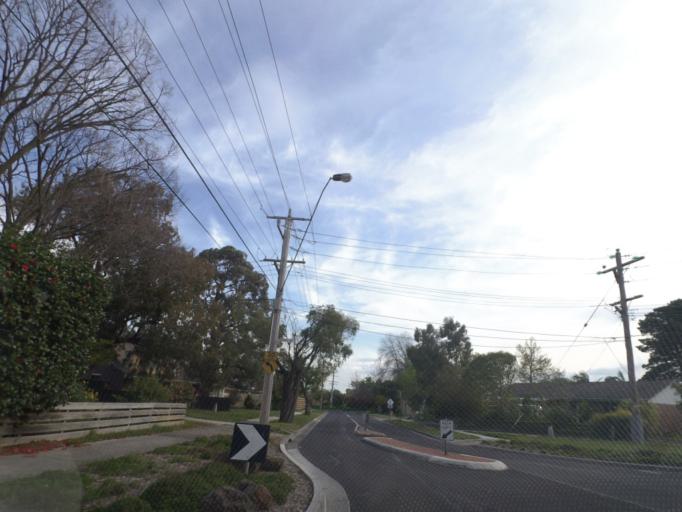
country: AU
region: Victoria
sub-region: Knox
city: Knoxfield
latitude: -37.8868
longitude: 145.2412
